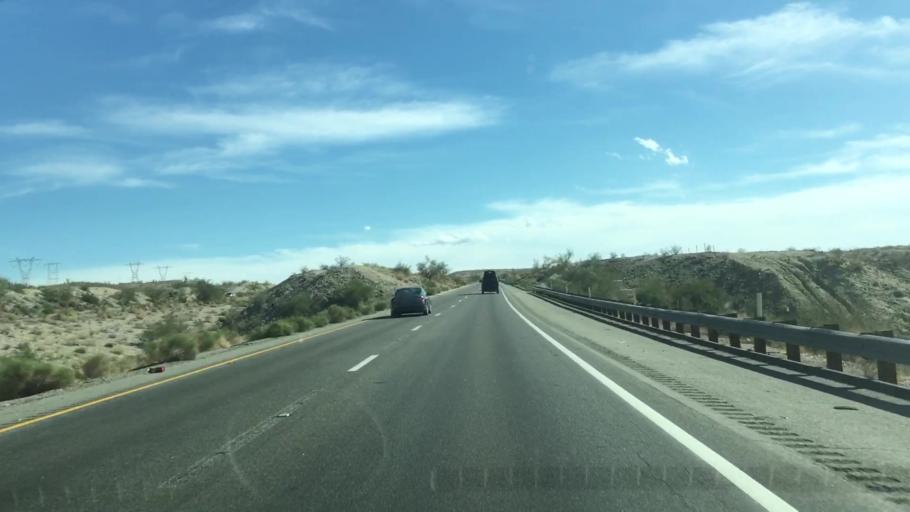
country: US
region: California
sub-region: Riverside County
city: Thermal
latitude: 33.6976
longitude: -116.0615
